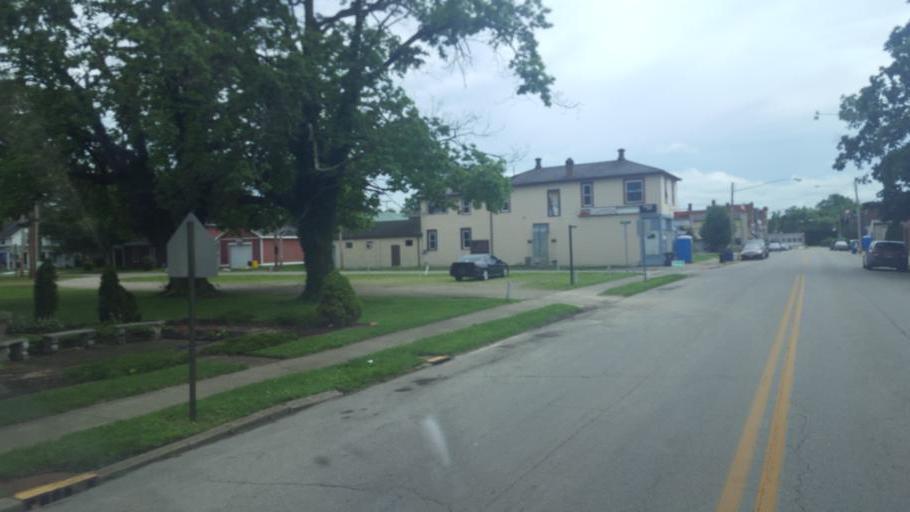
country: US
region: Ohio
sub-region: Pickaway County
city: Ashville
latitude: 39.7150
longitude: -82.9536
